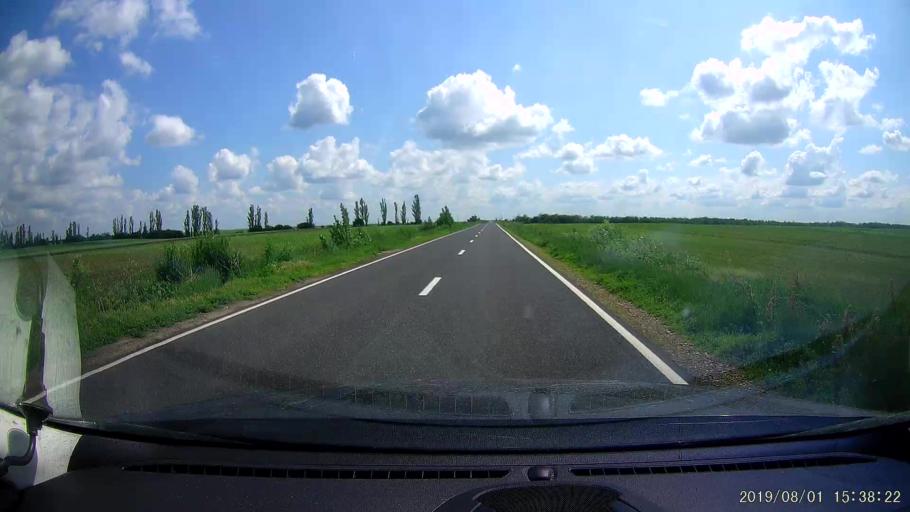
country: RO
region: Braila
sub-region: Comuna Insuratei
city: Insuratei
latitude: 44.8832
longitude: 27.5770
